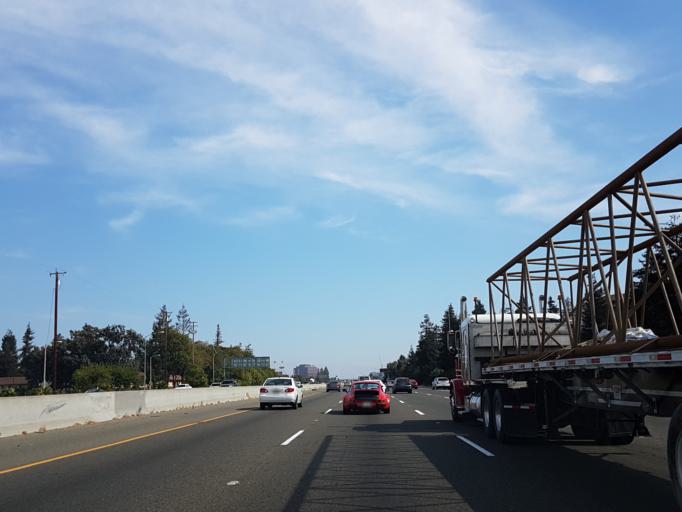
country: US
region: California
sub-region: Santa Clara County
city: Sunnyvale
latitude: 37.3905
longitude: -121.9939
